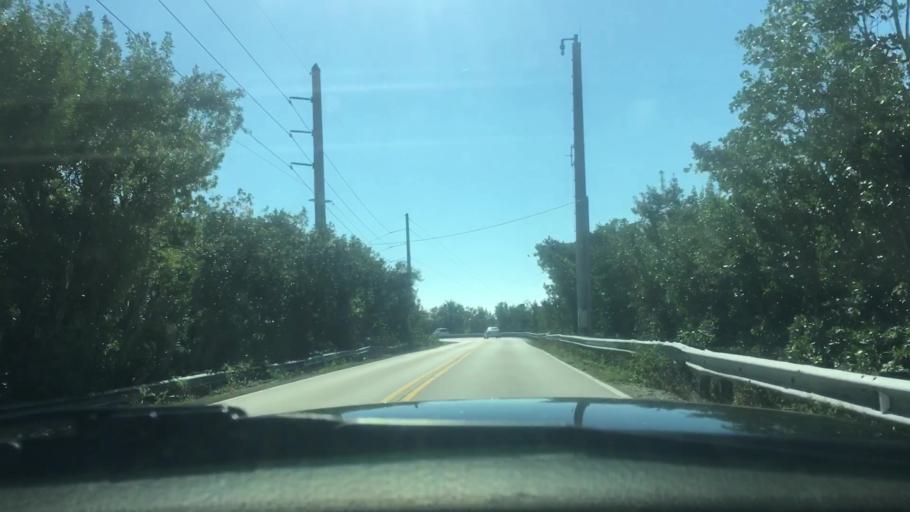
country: US
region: Florida
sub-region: Monroe County
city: North Key Largo
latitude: 25.2981
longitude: -80.3860
